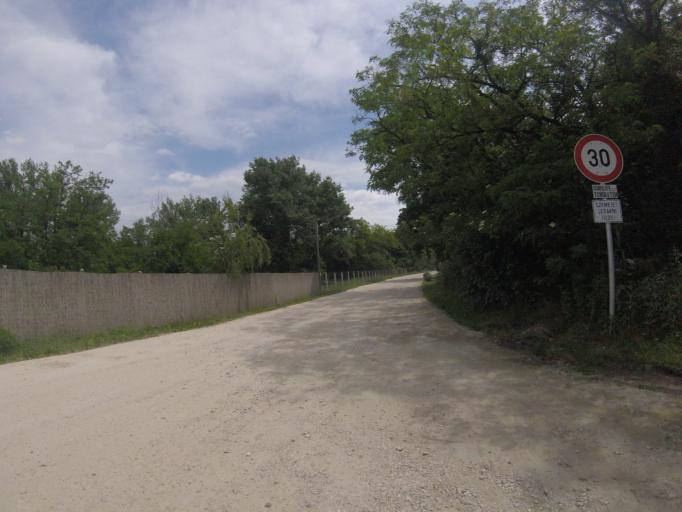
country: HU
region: Pest
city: Leanyfalu
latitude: 47.7202
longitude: 19.1050
